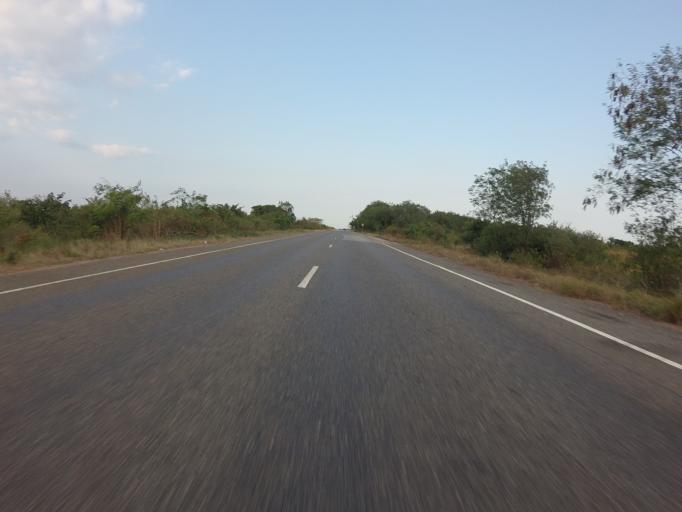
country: GH
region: Volta
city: Anloga
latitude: 6.0810
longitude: 0.5752
